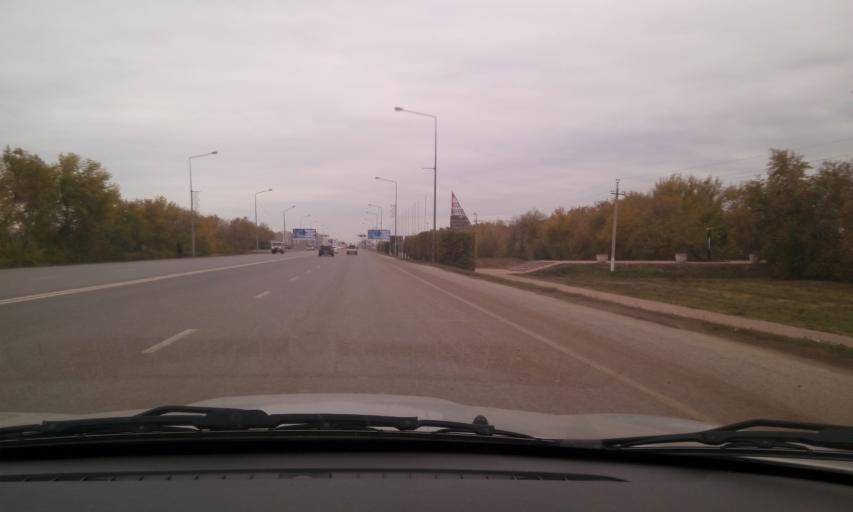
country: KZ
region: Astana Qalasy
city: Astana
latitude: 51.1105
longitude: 71.4100
